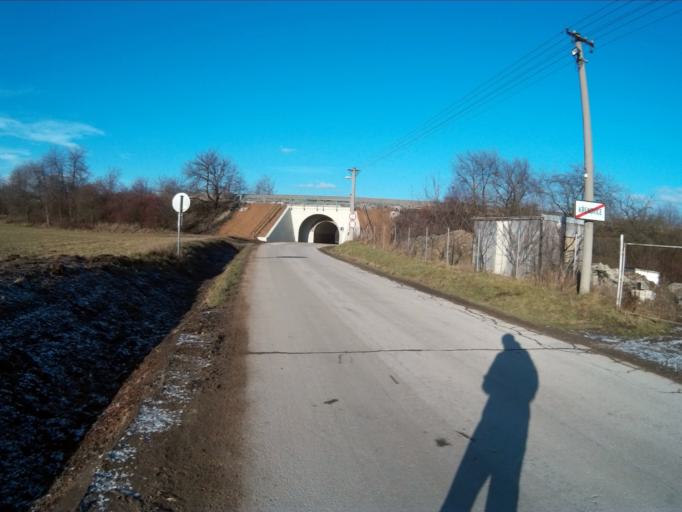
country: CZ
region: South Moravian
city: Krenovice
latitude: 49.1491
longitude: 16.8262
